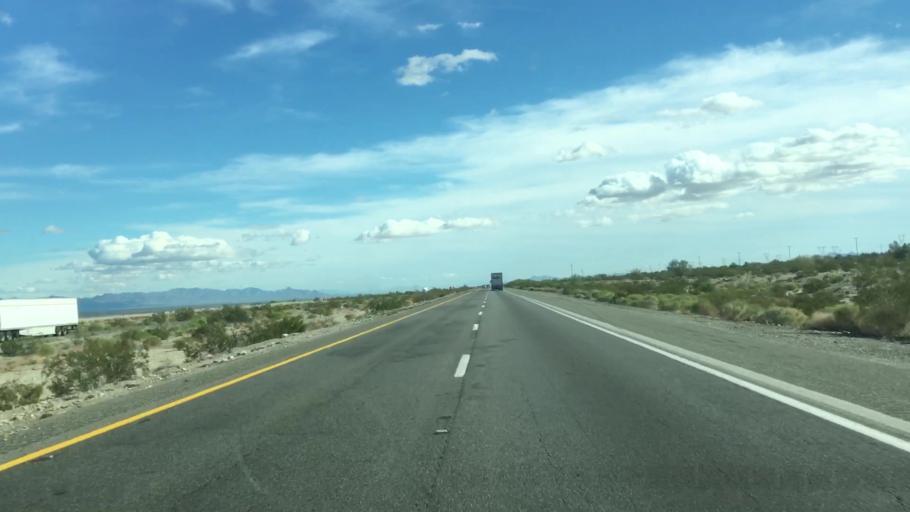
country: US
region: California
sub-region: Imperial County
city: Niland
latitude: 33.6912
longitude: -115.2738
